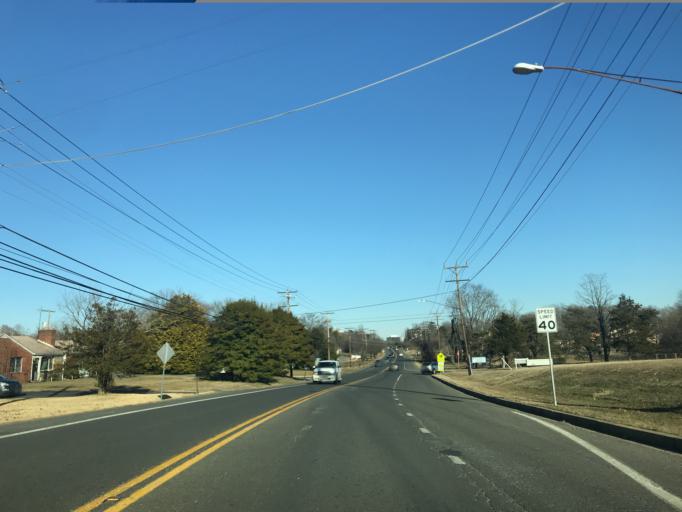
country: US
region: Maryland
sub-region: Prince George's County
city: Clinton
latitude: 38.7612
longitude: -76.9156
